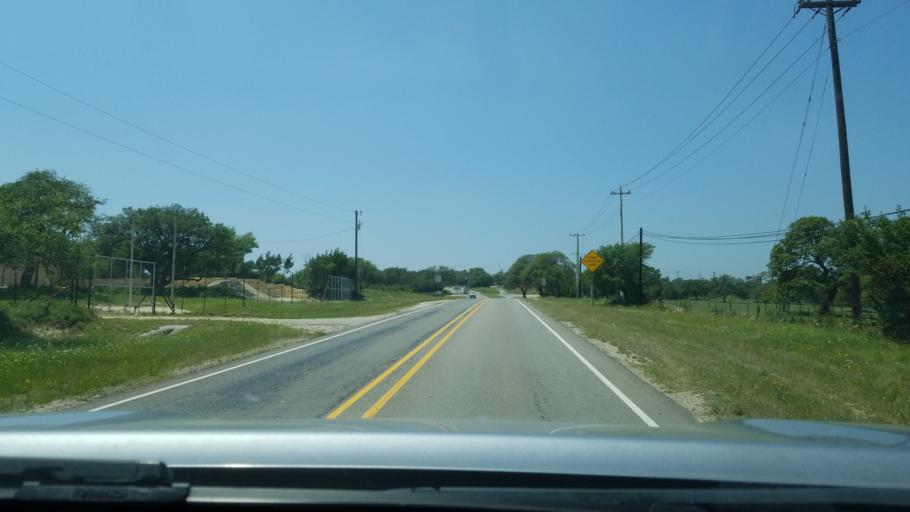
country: US
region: Texas
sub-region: Blanco County
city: Blanco
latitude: 30.0697
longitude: -98.4058
